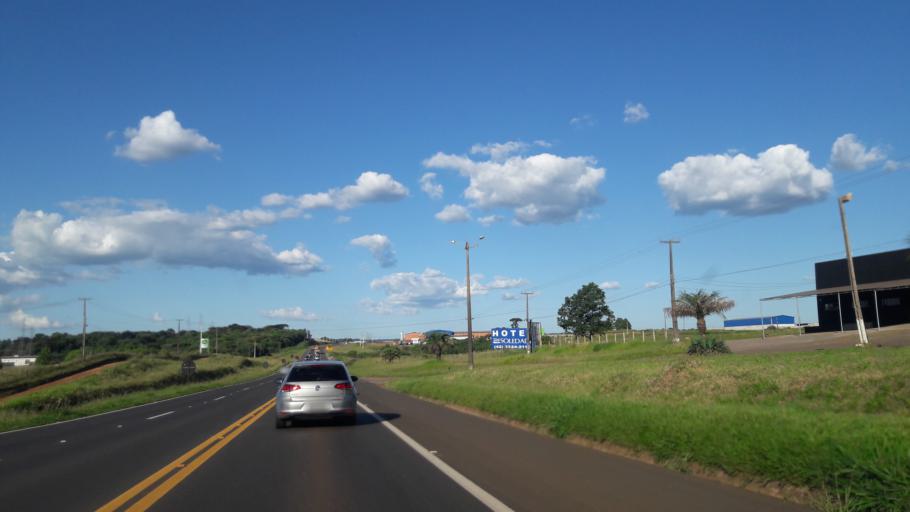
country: BR
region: Parana
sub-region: Guarapuava
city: Guarapuava
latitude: -25.3762
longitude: -51.5042
